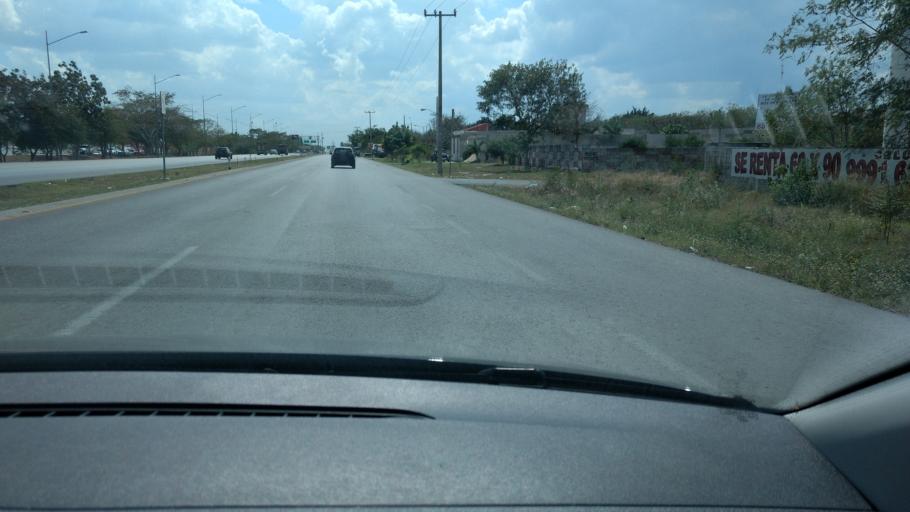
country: MX
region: Yucatan
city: Merida
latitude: 20.9940
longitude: -89.5624
